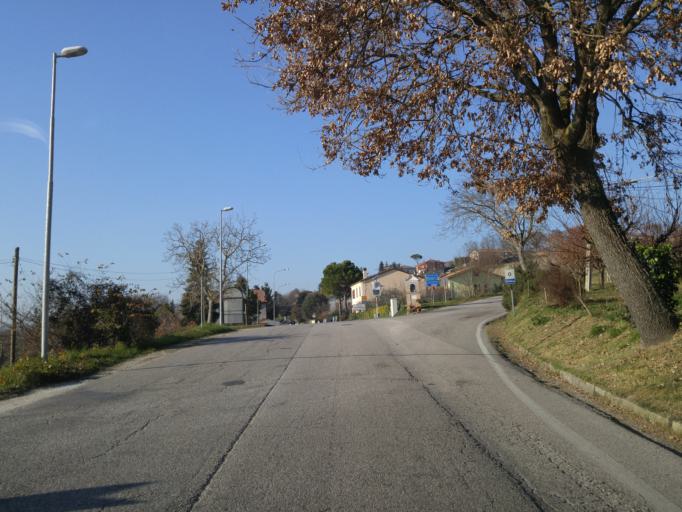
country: IT
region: The Marches
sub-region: Provincia di Pesaro e Urbino
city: Montefelcino
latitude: 43.7220
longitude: 12.8414
